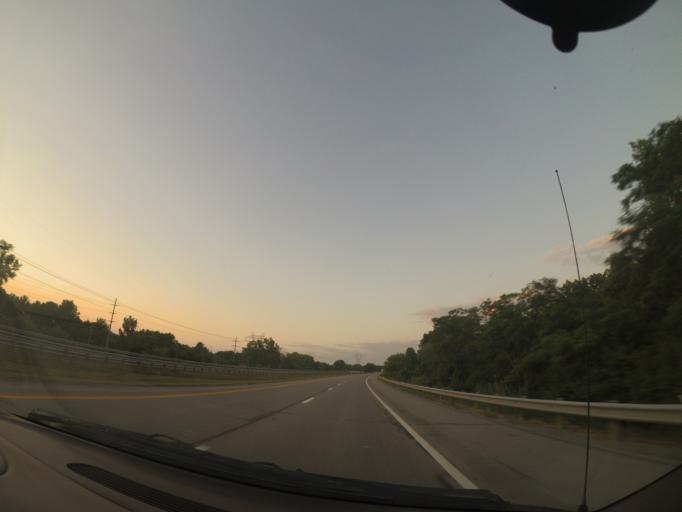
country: US
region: Ohio
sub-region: Lake County
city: Painesville
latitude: 41.7341
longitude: -81.2544
